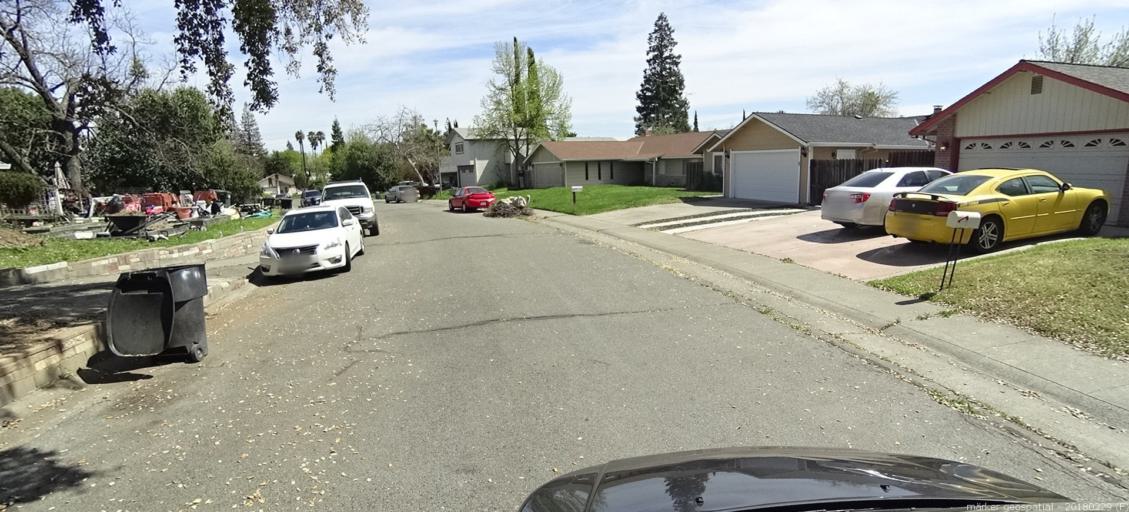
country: US
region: California
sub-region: Sacramento County
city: Rosemont
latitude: 38.5501
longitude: -121.3466
